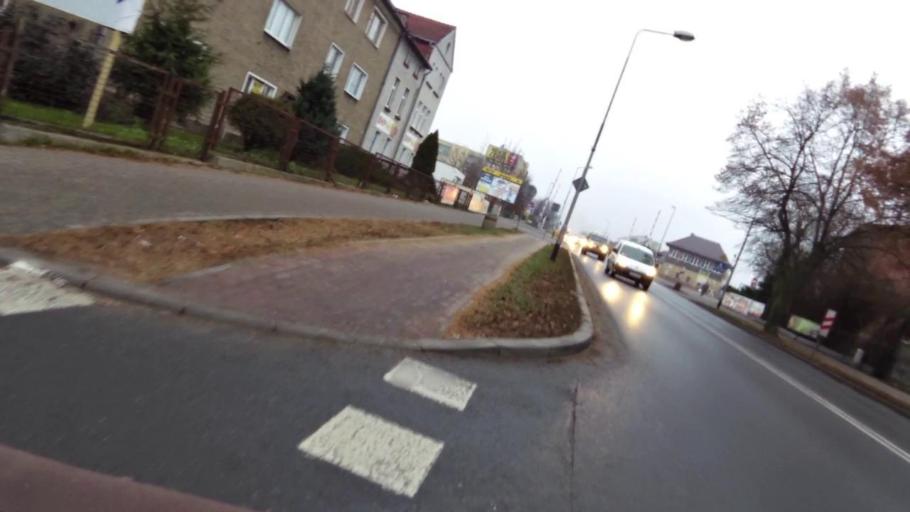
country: PL
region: West Pomeranian Voivodeship
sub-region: Powiat walecki
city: Walcz
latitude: 53.2763
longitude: 16.4826
